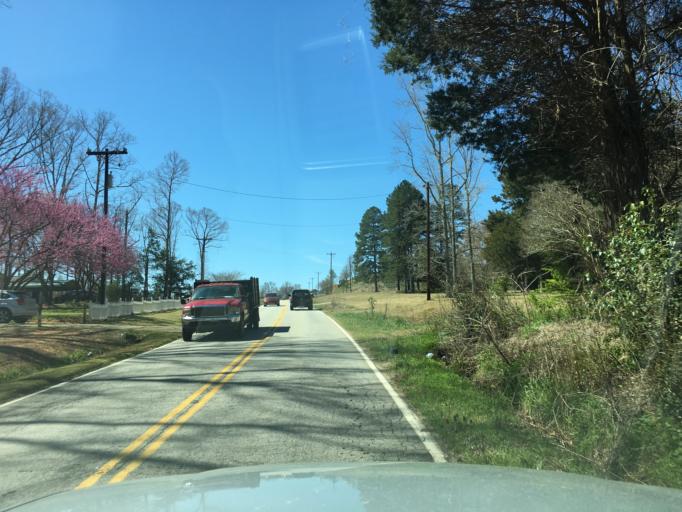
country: US
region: South Carolina
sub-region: Spartanburg County
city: Roebuck
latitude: 34.8975
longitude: -81.9641
